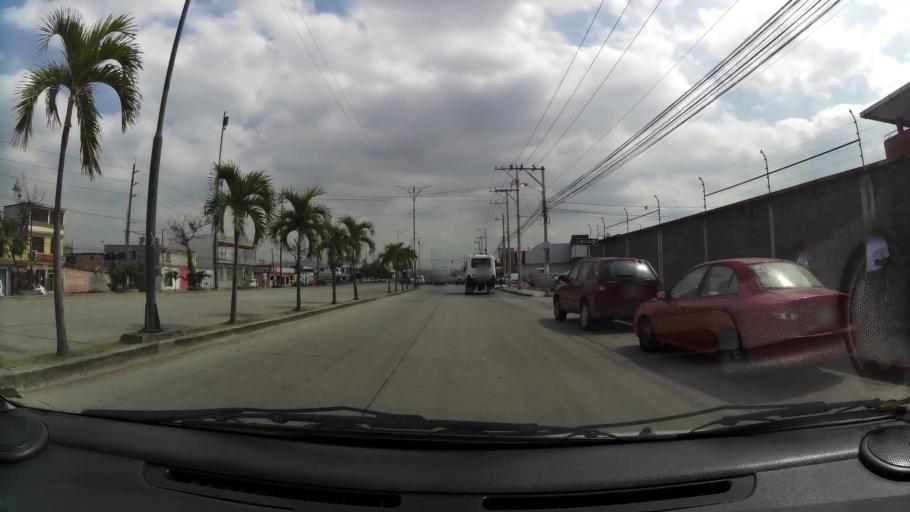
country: EC
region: Guayas
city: Eloy Alfaro
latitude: -2.0841
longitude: -79.9188
